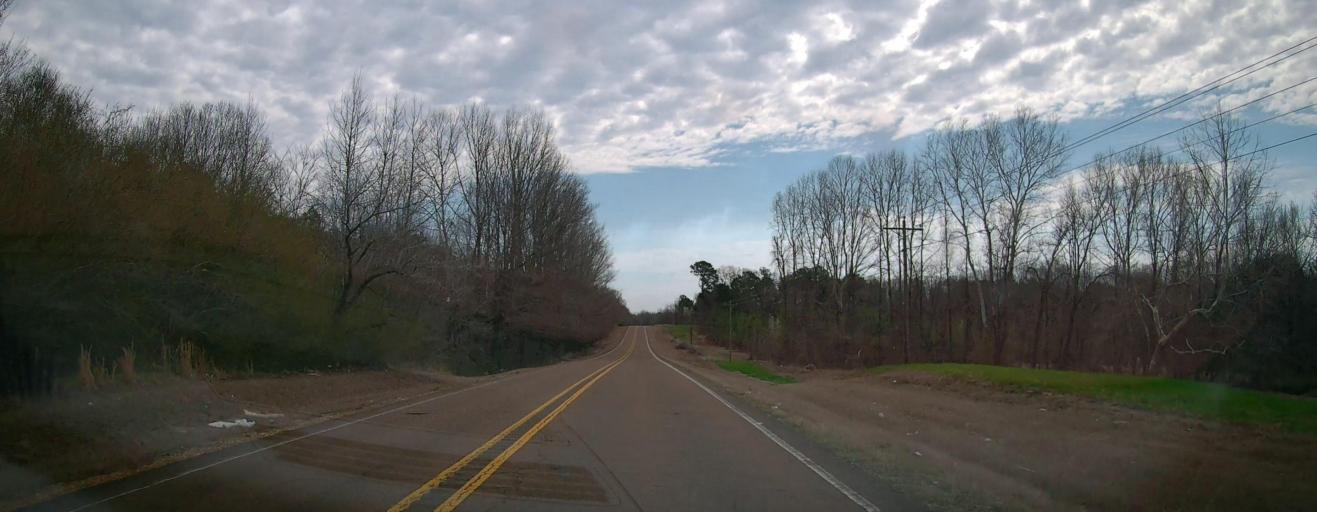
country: US
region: Mississippi
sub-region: Marshall County
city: Byhalia
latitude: 34.8523
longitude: -89.6356
